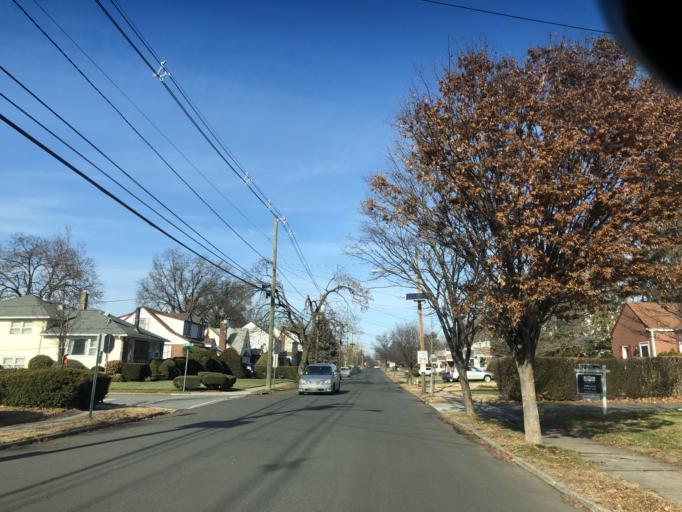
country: US
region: New Jersey
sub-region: Bergen County
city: Elmwood Park
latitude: 40.9226
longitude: -74.1179
